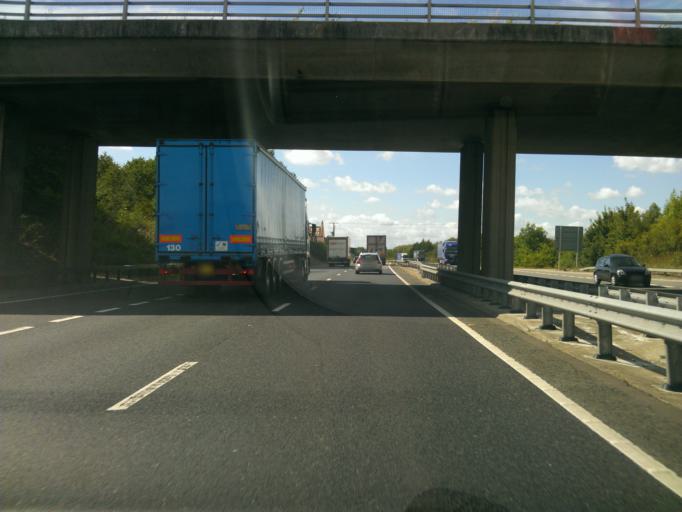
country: GB
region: England
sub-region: Bedford
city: Pertenhall
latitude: 52.3596
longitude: -0.4057
